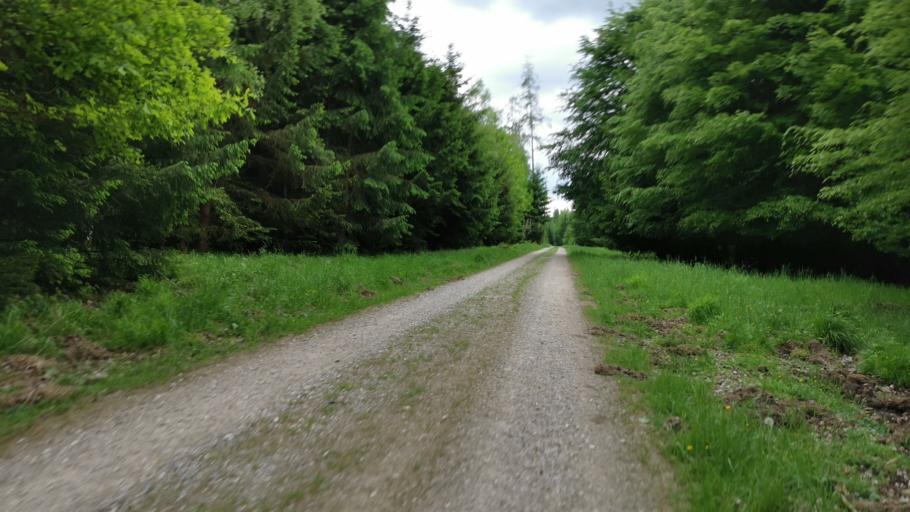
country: DE
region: Bavaria
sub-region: Upper Bavaria
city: Baierbrunn
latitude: 48.0345
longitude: 11.4662
